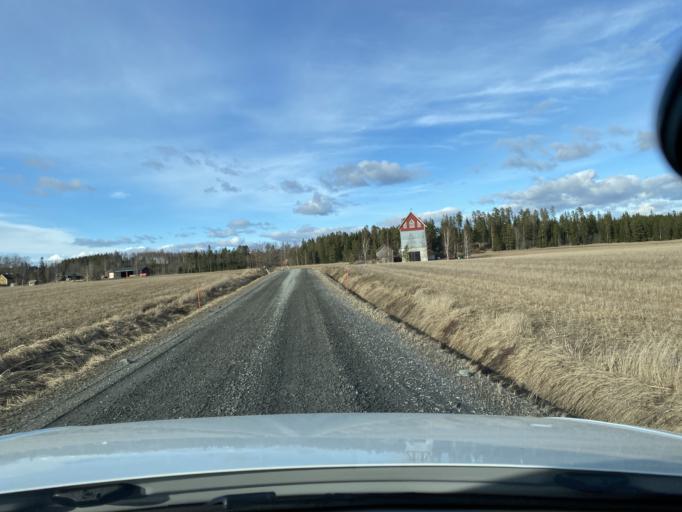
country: FI
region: Pirkanmaa
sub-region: Lounais-Pirkanmaa
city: Punkalaidun
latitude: 61.1349
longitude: 23.2078
